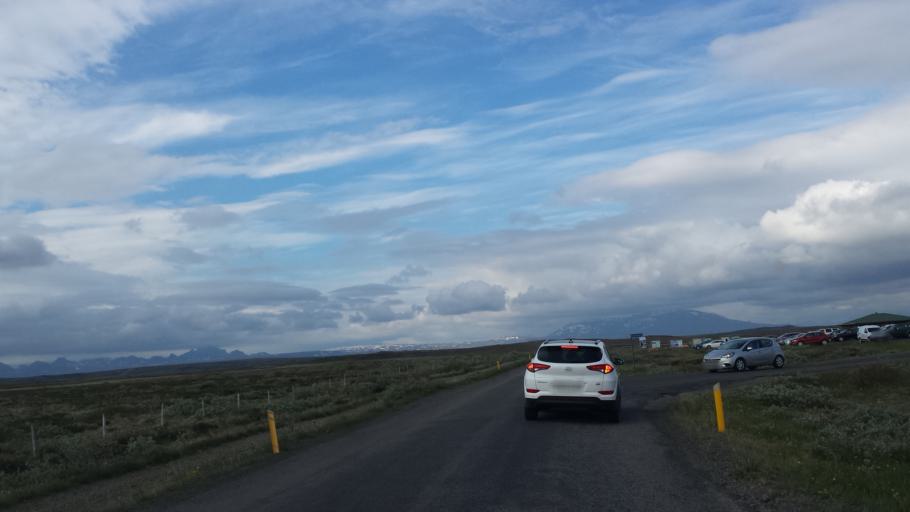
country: IS
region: South
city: Vestmannaeyjar
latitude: 64.3246
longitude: -20.1329
